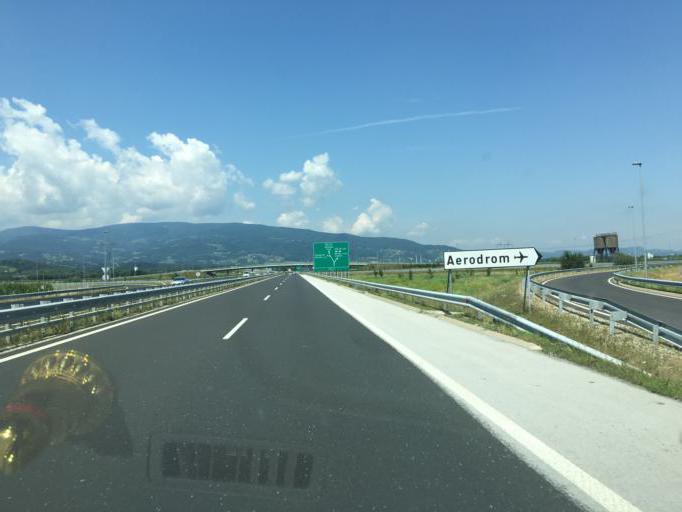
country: SI
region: Hoce-Slivnica
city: Hotinja Vas
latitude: 46.4725
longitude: 15.6792
